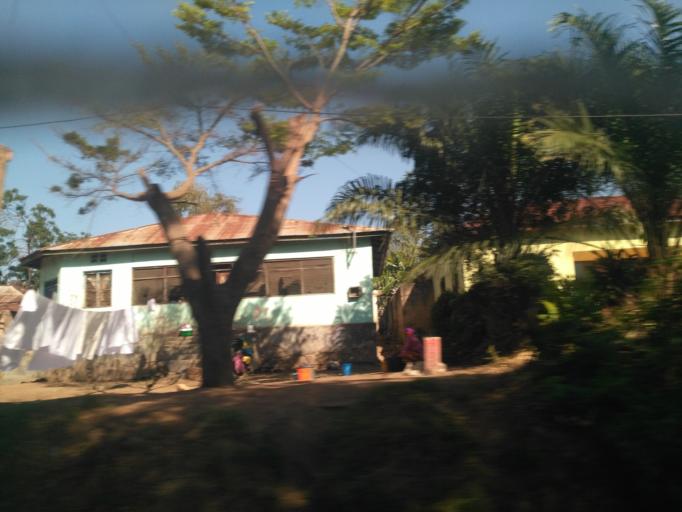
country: TZ
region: Mwanza
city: Mwanza
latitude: -2.5011
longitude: 32.8963
